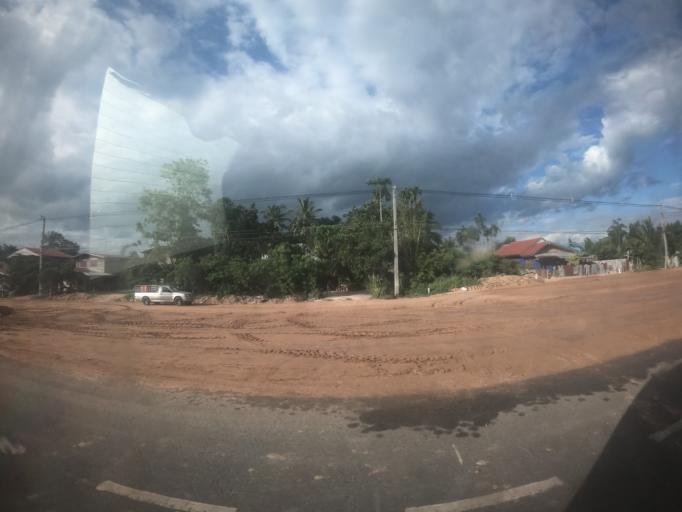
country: TH
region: Surin
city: Kap Choeng
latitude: 14.4810
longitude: 103.5845
